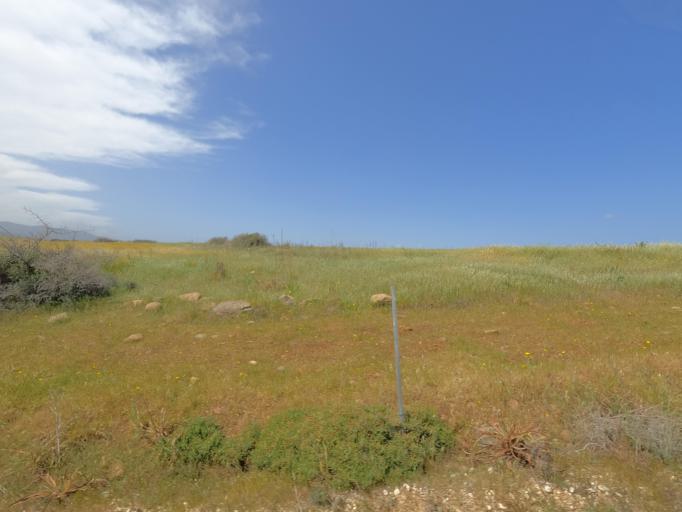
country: CY
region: Lefkosia
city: Lefka
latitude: 35.1008
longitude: 32.9396
